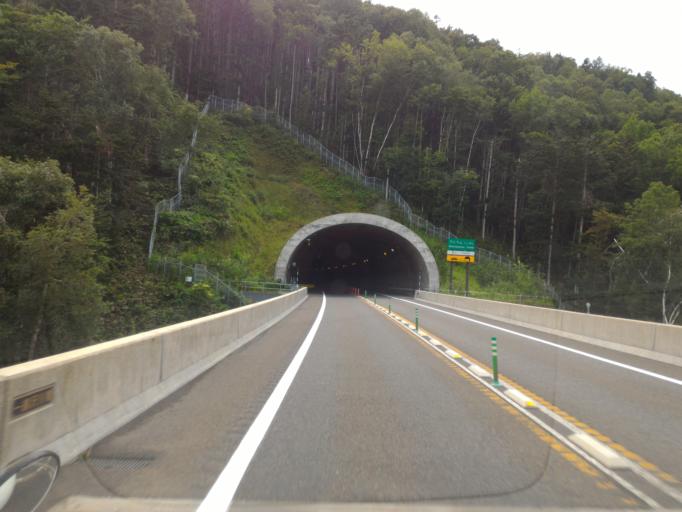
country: JP
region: Hokkaido
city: Shimo-furano
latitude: 43.0660
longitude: 142.5316
